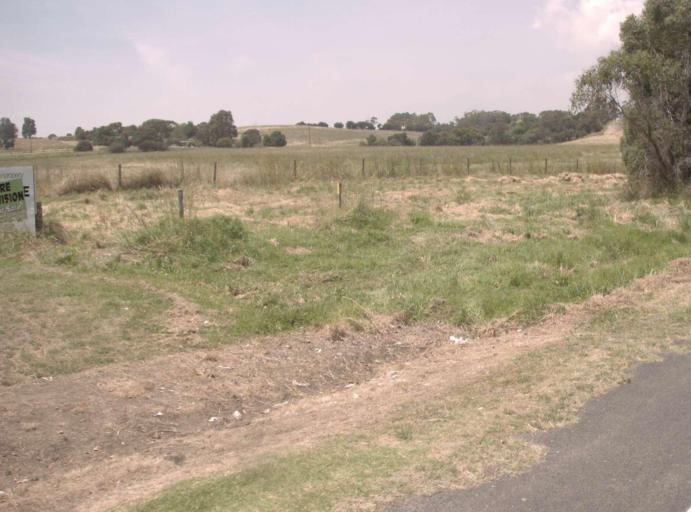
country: AU
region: Victoria
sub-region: Latrobe
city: Traralgon
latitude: -38.2128
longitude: 146.5460
